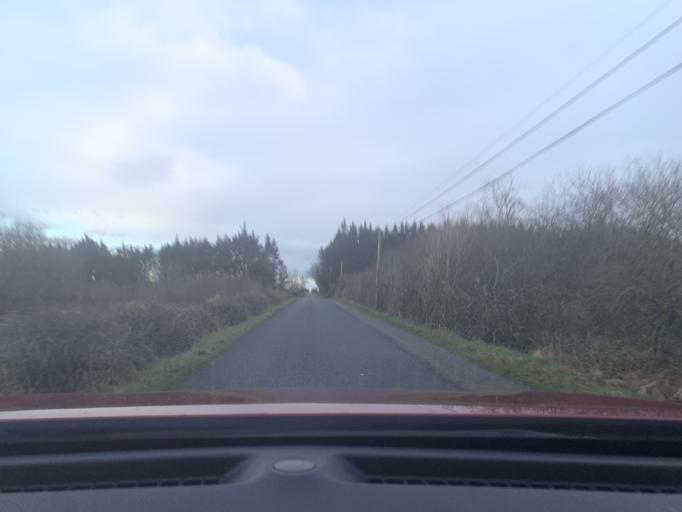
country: IE
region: Connaught
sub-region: Roscommon
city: Ballaghaderreen
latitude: 53.8829
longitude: -8.5659
